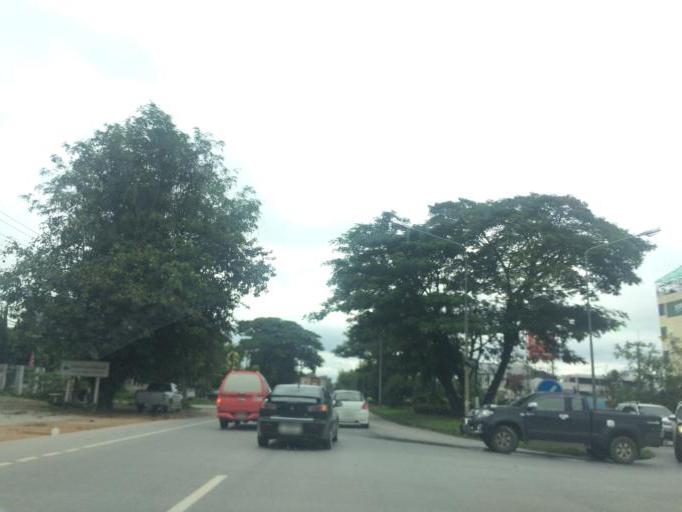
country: TH
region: Chiang Rai
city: Chiang Rai
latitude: 19.8640
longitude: 99.8220
